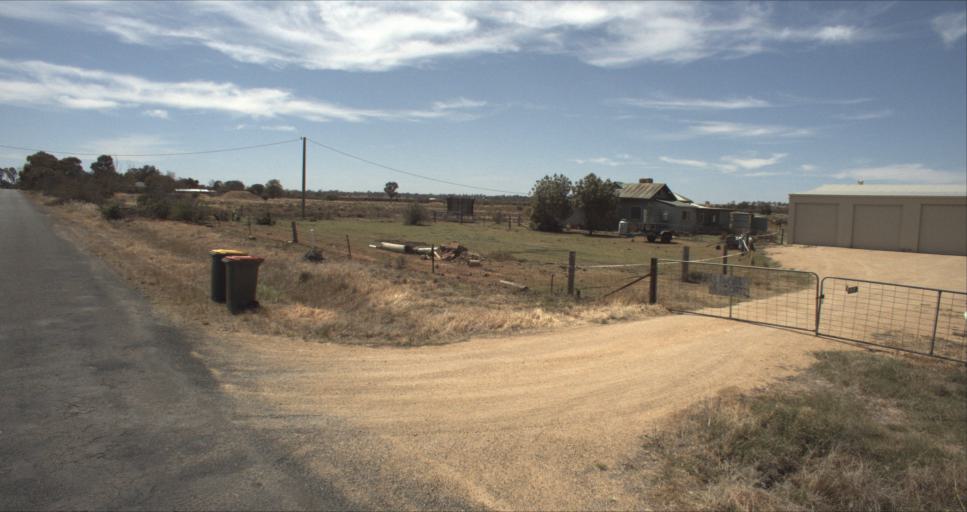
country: AU
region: New South Wales
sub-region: Leeton
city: Leeton
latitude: -34.5987
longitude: 146.4274
